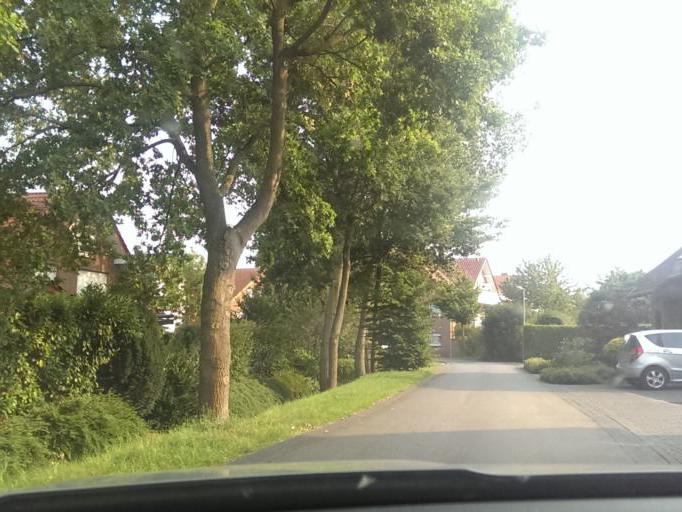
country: DE
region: North Rhine-Westphalia
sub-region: Regierungsbezirk Detmold
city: Delbruck
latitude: 51.7715
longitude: 8.5714
